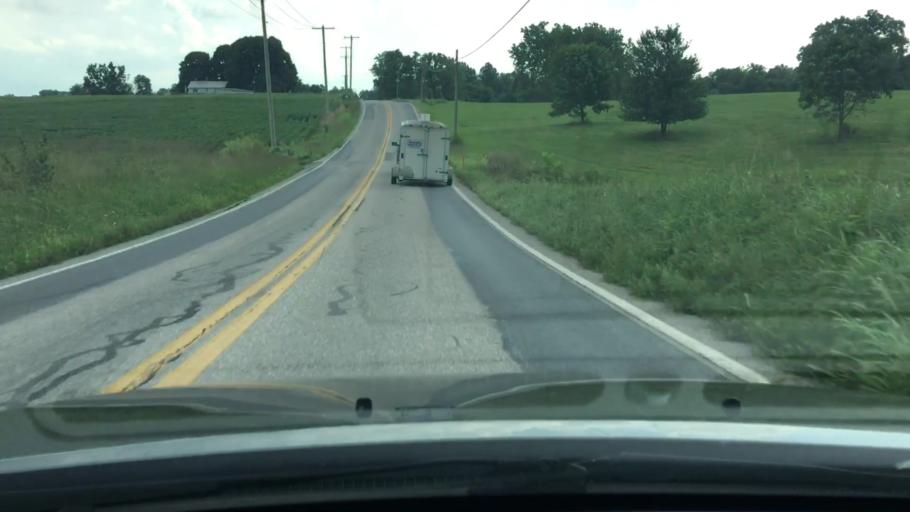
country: US
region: Pennsylvania
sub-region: Franklin County
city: Scotland
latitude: 39.9591
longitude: -77.5835
